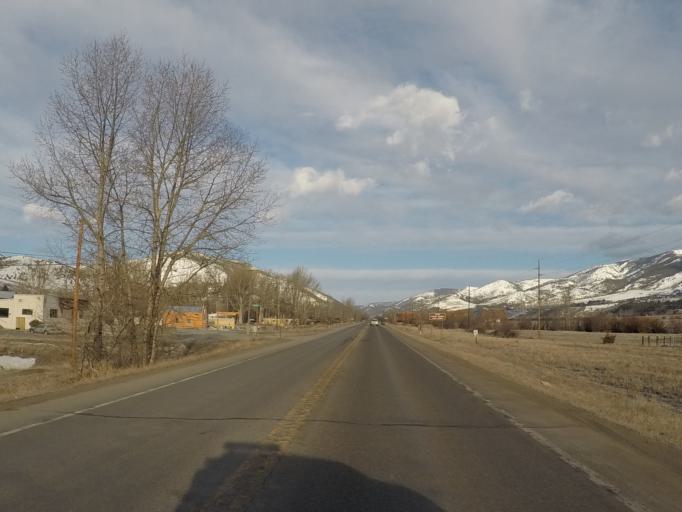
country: US
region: Montana
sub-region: Deer Lodge County
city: Anaconda
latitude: 46.1414
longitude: -112.9889
